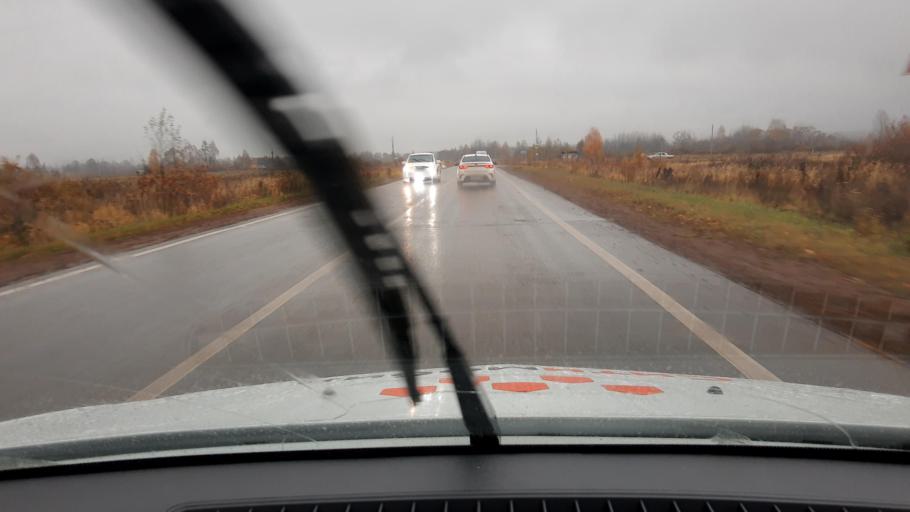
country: RU
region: Bashkortostan
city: Kabakovo
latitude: 54.7337
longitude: 56.1979
